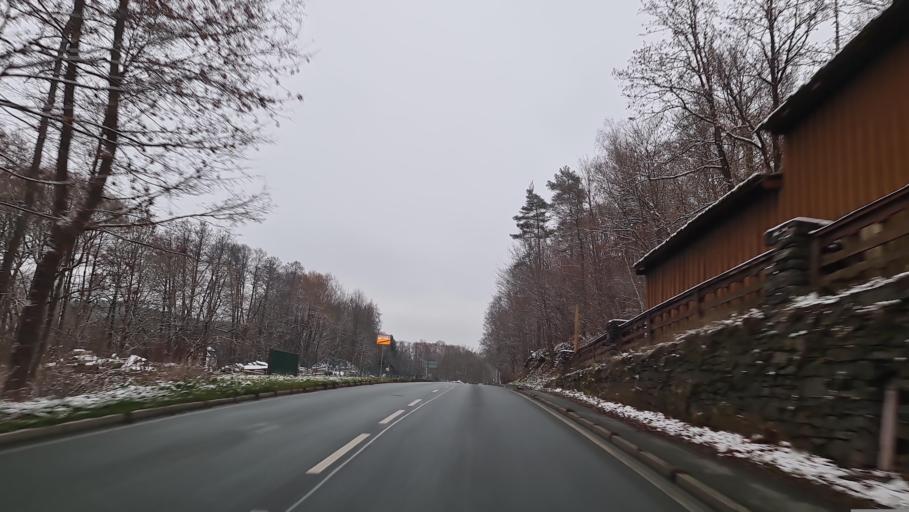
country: DE
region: Saxony
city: Markneukirchen
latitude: 50.3100
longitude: 12.3074
